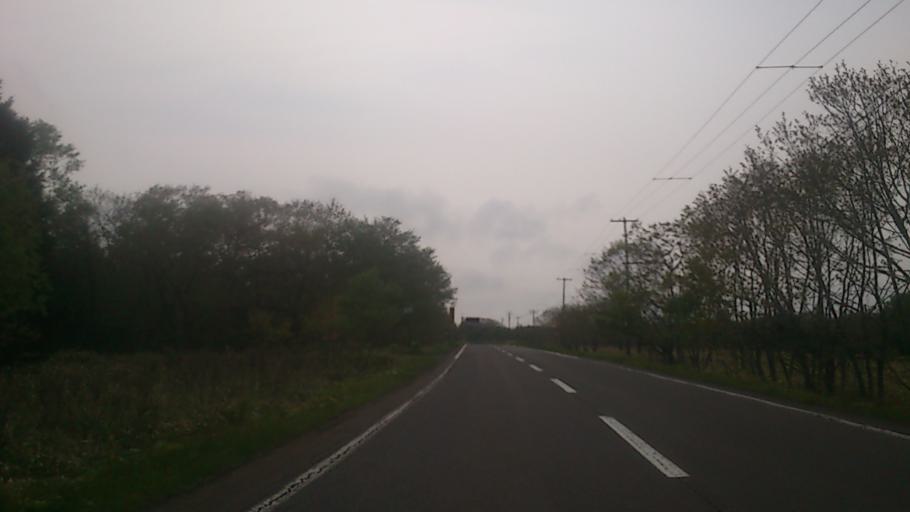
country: JP
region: Hokkaido
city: Nemuro
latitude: 43.2077
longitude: 145.3327
